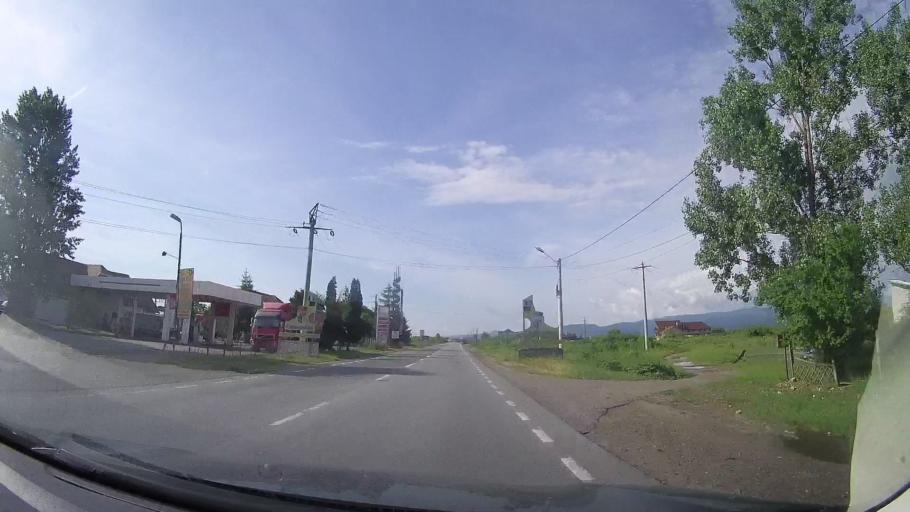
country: RO
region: Caras-Severin
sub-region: Municipiul Caransebes
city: Caransebes
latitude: 45.4364
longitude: 22.1937
